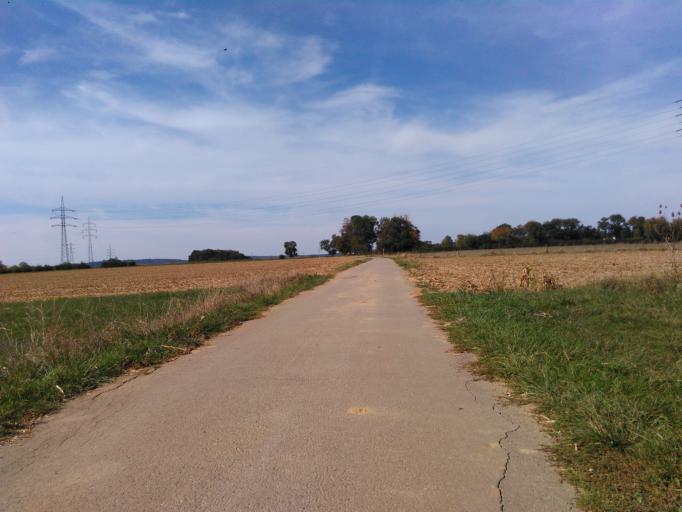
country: LU
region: Luxembourg
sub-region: Canton d'Esch-sur-Alzette
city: Sanem
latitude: 49.5378
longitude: 5.9284
